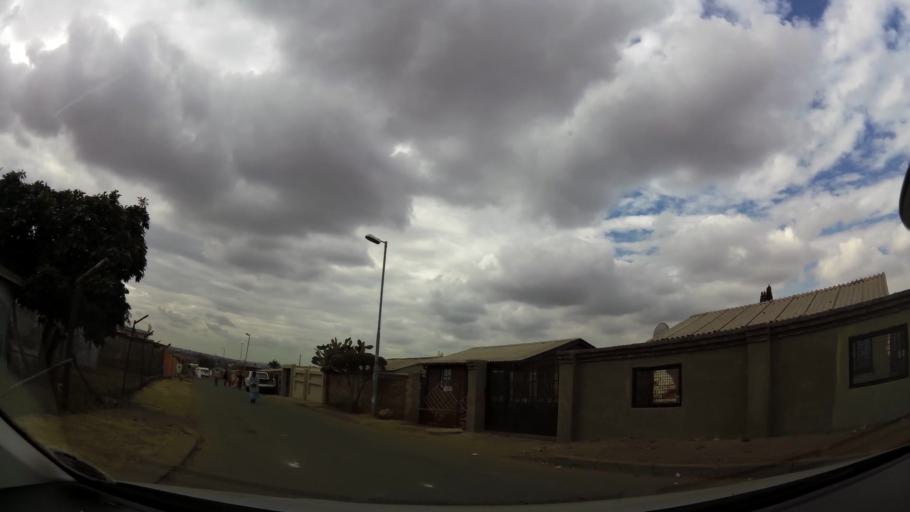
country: ZA
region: Gauteng
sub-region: City of Johannesburg Metropolitan Municipality
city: Soweto
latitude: -26.2697
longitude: 27.8618
